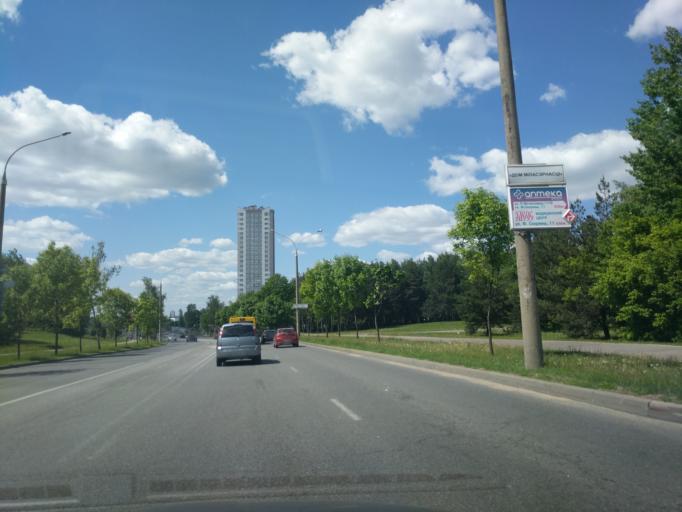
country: BY
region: Minsk
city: Borovlyany
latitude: 53.9265
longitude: 27.6592
